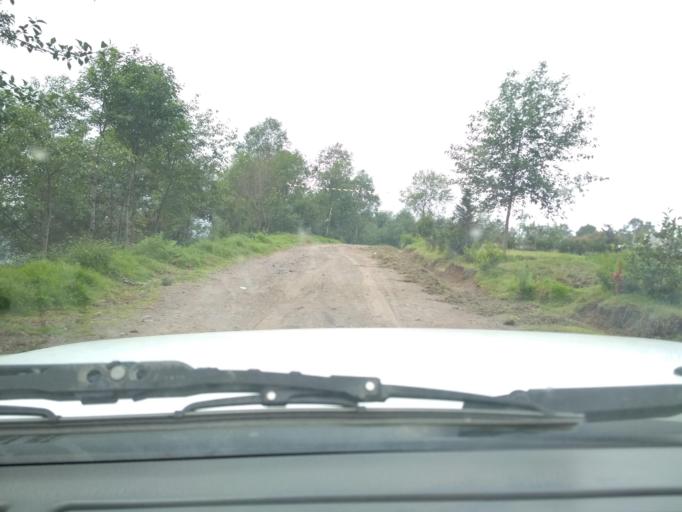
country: MX
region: Veracruz
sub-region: La Perla
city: Chilapa
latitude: 18.9913
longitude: -97.1632
